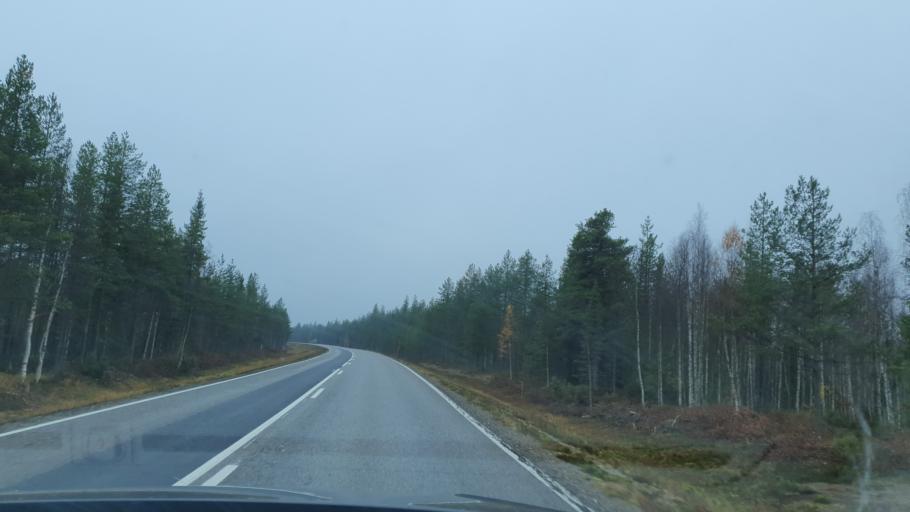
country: FI
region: Lapland
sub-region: Tunturi-Lappi
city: Kittilae
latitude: 67.3731
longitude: 24.8925
